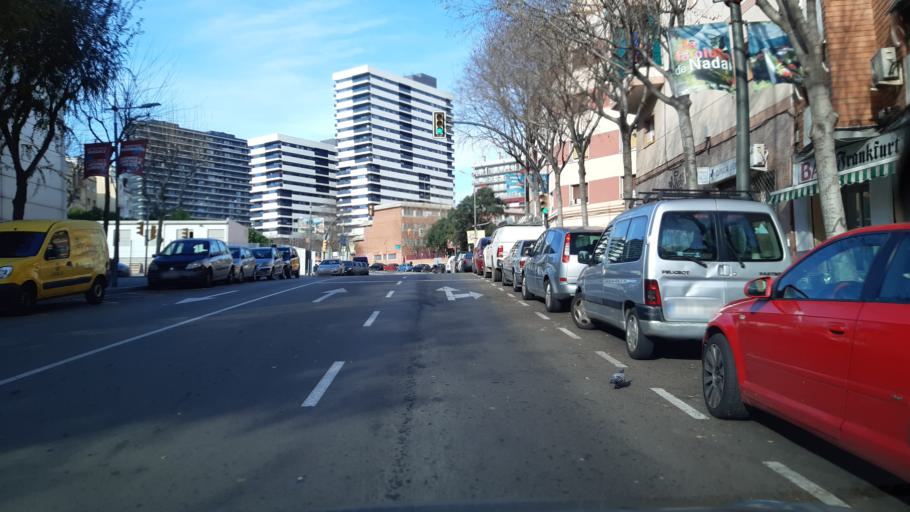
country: ES
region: Catalonia
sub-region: Provincia de Barcelona
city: L'Hospitalet de Llobregat
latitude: 41.3736
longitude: 2.1123
